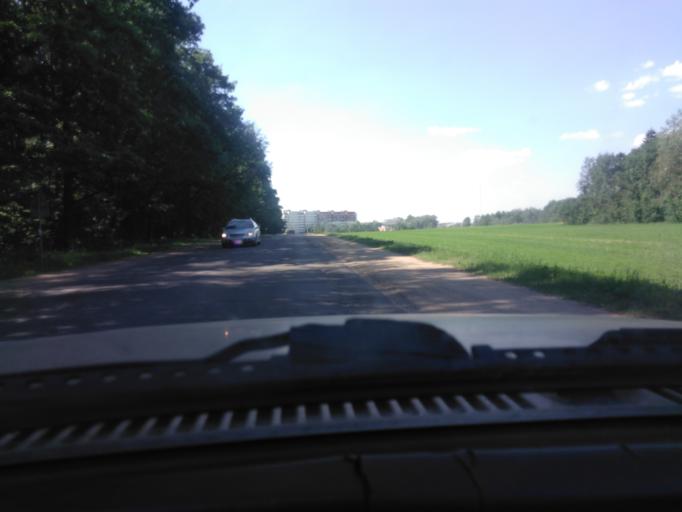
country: BY
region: Mogilev
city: Palykavichy Pyershyya
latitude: 53.9537
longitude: 30.3694
